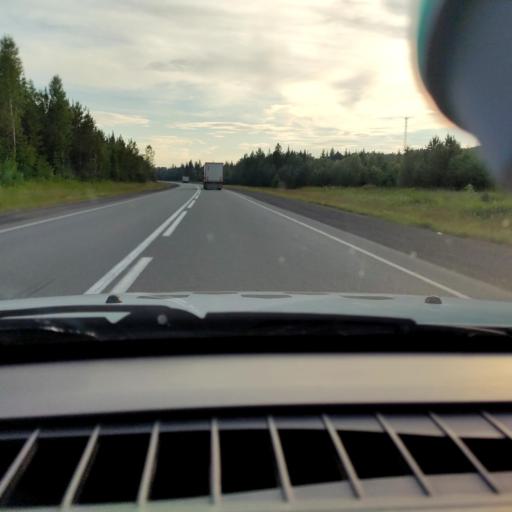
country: RU
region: Sverdlovsk
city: Arti
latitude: 56.7954
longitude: 58.4702
